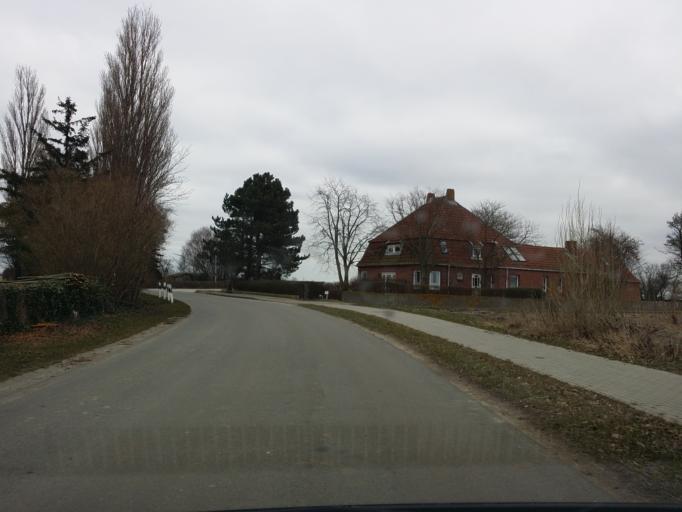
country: DE
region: Schleswig-Holstein
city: Grossenbrode
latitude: 54.4887
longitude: 11.0305
